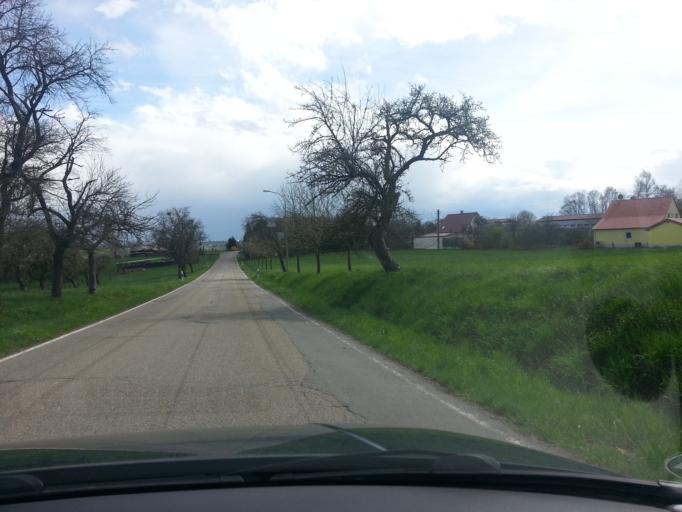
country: DE
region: Rheinland-Pfalz
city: Massweiler
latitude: 49.2681
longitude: 7.5311
